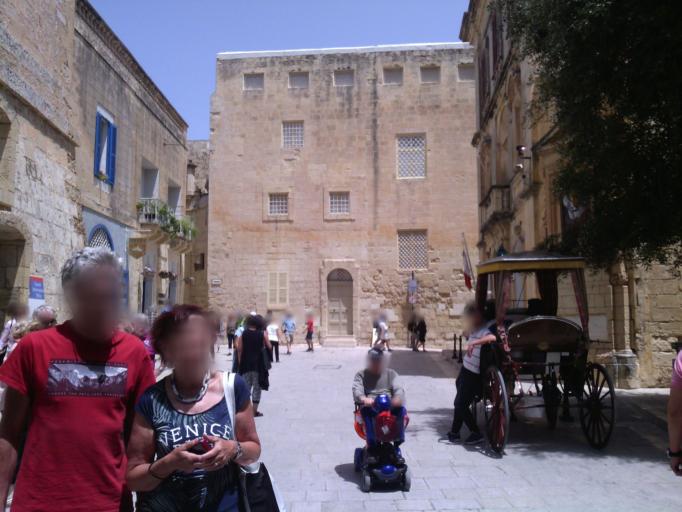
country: MT
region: L-Imdina
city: Imdina
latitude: 35.8847
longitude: 14.4033
